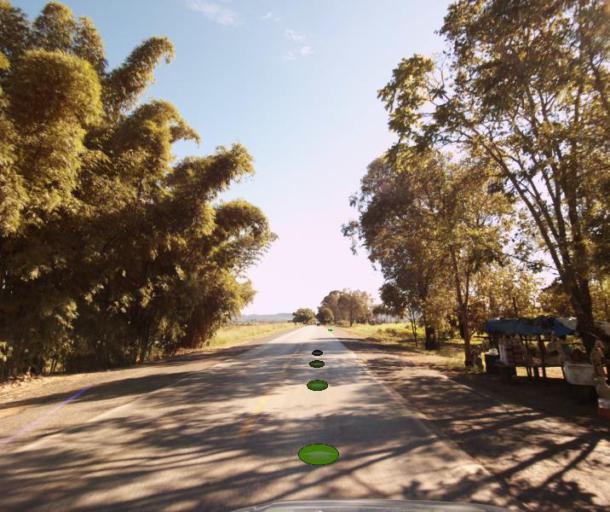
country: BR
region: Goias
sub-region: Uruacu
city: Uruacu
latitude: -14.6300
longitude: -49.1741
